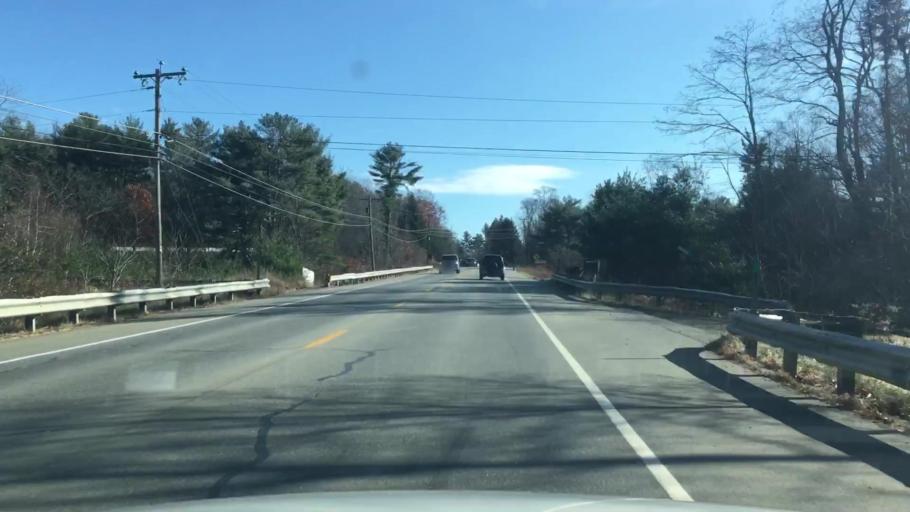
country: US
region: Maine
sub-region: Kennebec County
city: Windsor
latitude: 44.2717
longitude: -69.5850
